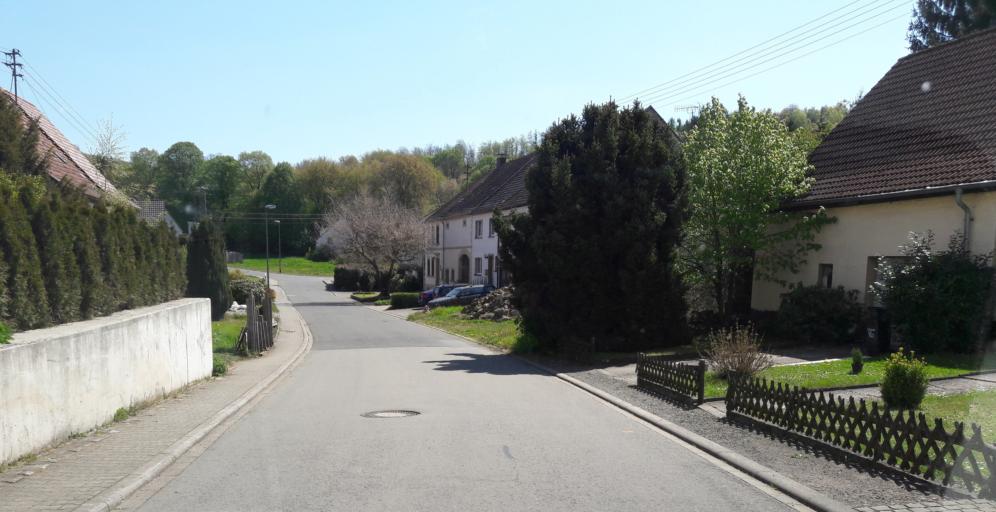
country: DE
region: Rheinland-Pfalz
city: Pfeffelbach
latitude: 49.5387
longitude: 7.3298
